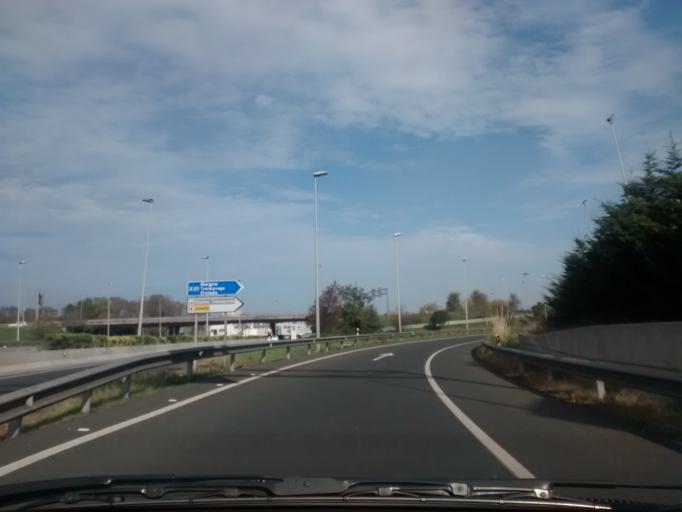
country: ES
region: Cantabria
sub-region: Provincia de Cantabria
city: El Astillero
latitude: 43.4386
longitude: -3.8368
